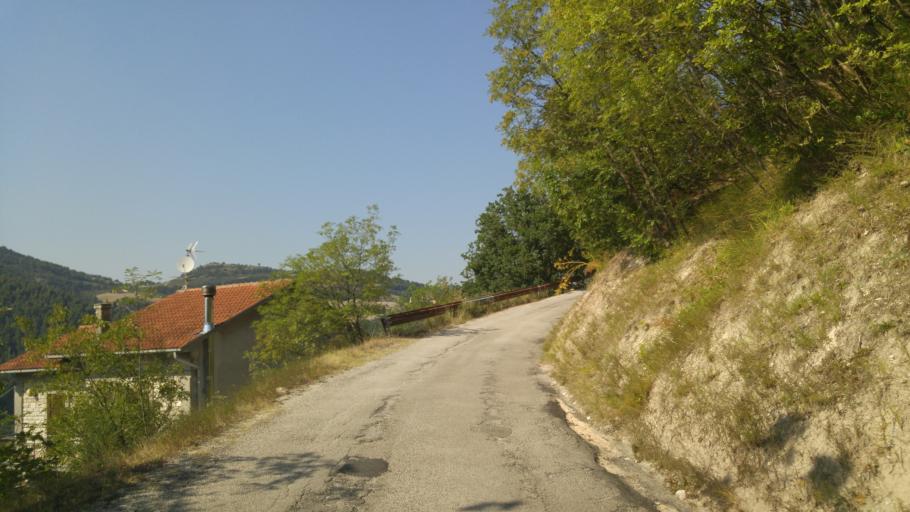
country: IT
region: The Marches
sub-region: Provincia di Pesaro e Urbino
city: Fossombrone
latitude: 43.6802
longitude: 12.8034
